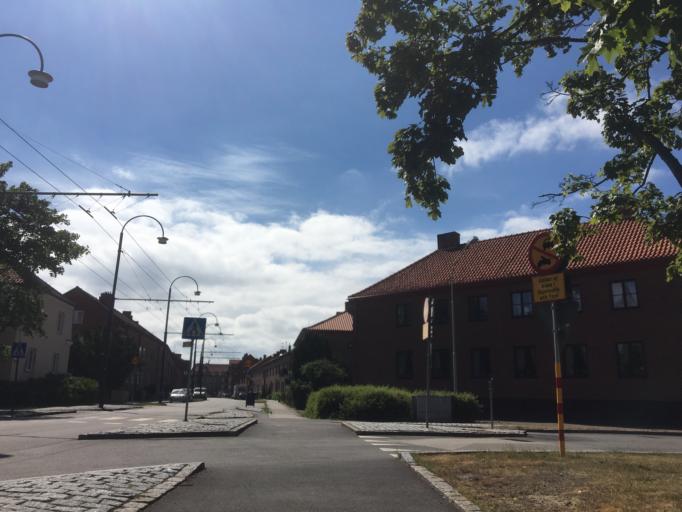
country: SE
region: Skane
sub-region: Landskrona
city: Landskrona
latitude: 55.8793
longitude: 12.8381
